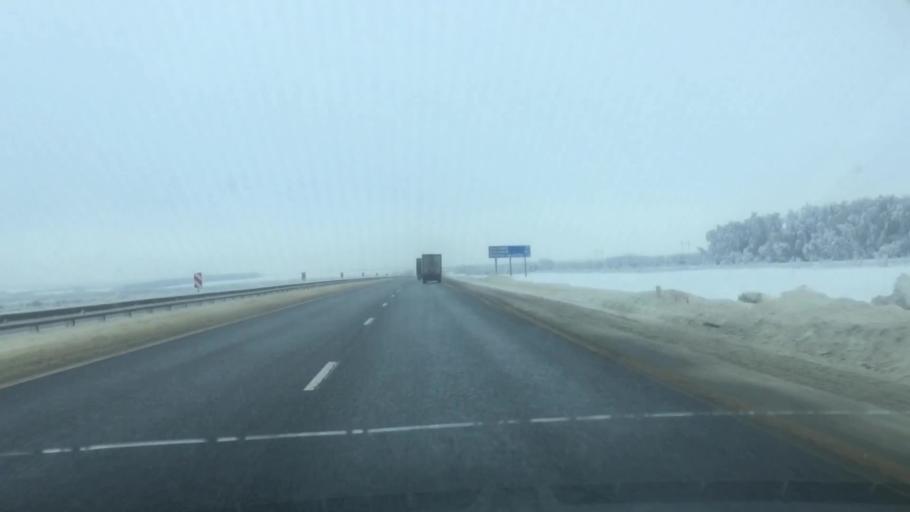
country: RU
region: Lipetsk
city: Stanovoye
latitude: 52.7424
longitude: 38.4732
